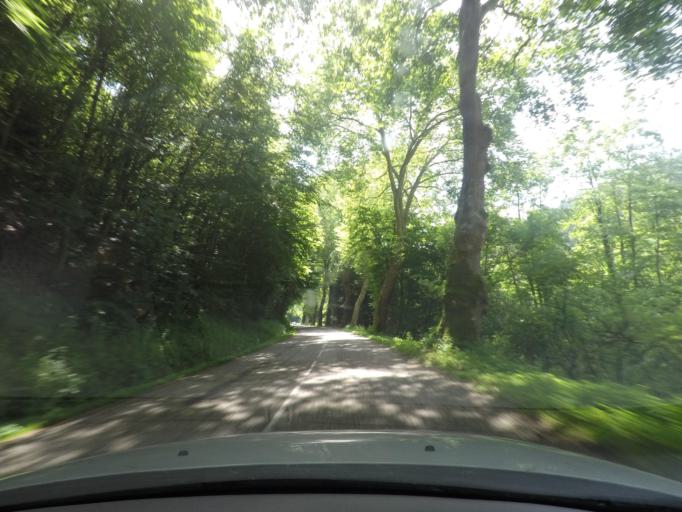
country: FR
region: Lorraine
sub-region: Departement de la Moselle
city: Phalsbourg
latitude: 48.8139
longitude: 7.2879
